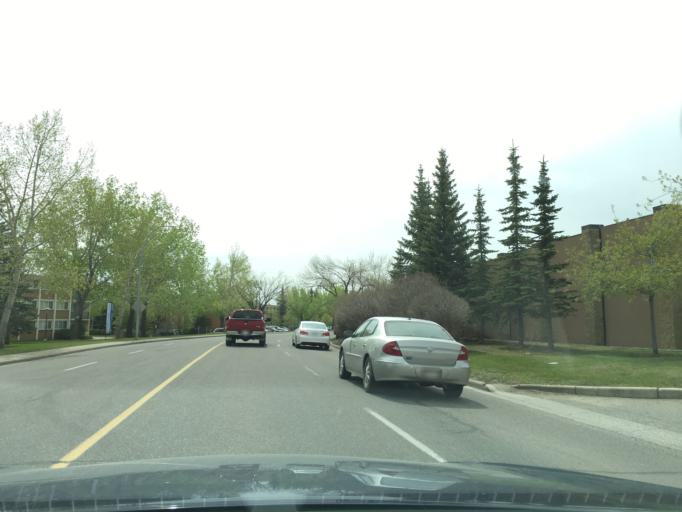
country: CA
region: Alberta
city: Calgary
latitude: 50.9678
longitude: -114.0684
